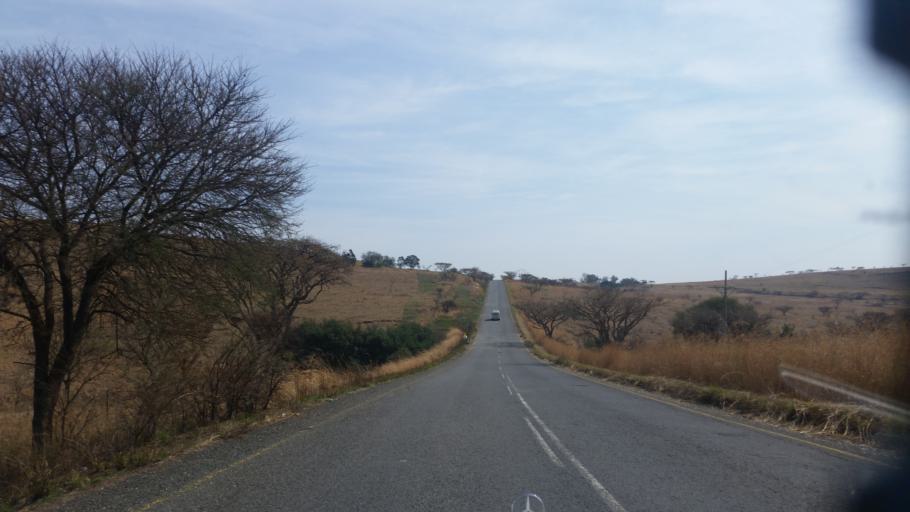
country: ZA
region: KwaZulu-Natal
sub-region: uThukela District Municipality
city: Estcourt
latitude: -29.0696
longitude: 29.9396
